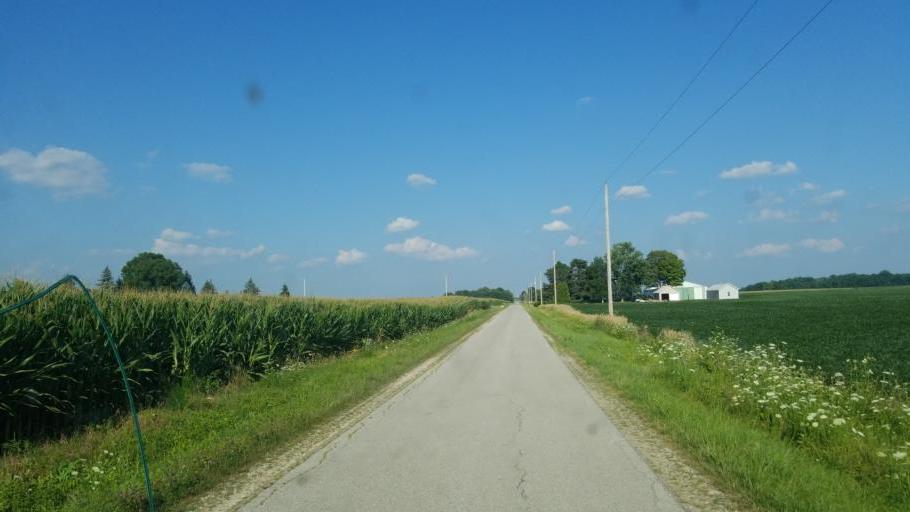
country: US
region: Ohio
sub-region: Crawford County
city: Bucyrus
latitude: 40.7897
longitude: -83.1029
